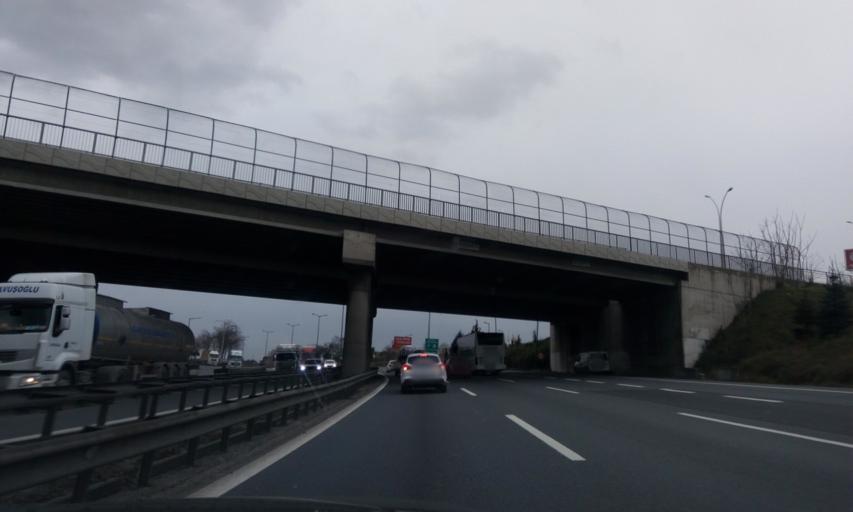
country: TR
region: Kocaeli
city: Izmit
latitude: 40.7837
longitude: 29.9305
